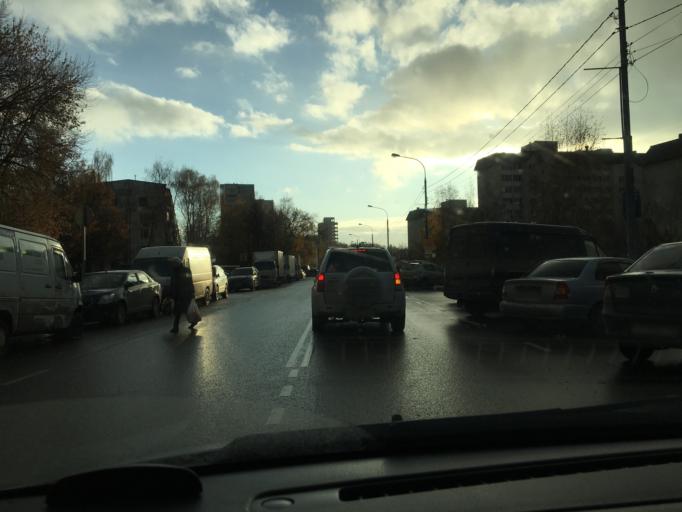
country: RU
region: Moskovskaya
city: Vidnoye
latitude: 55.5510
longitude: 37.7031
